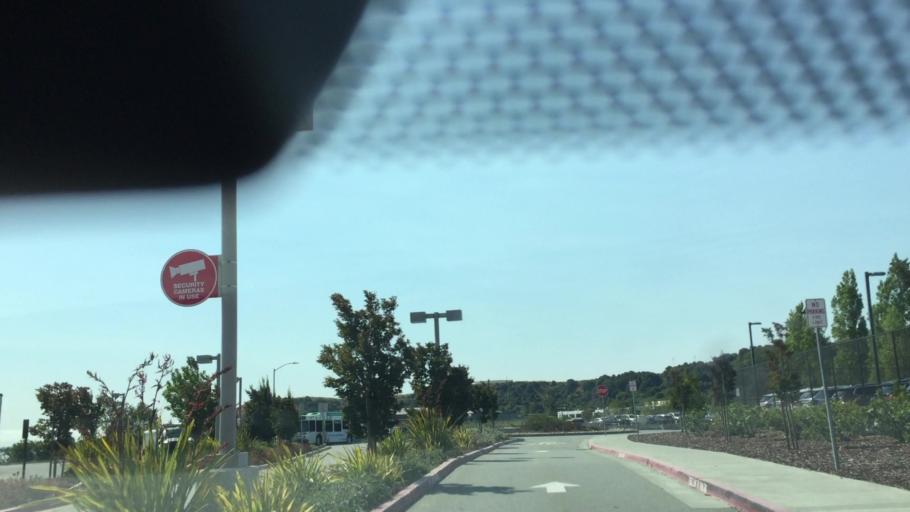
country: US
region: California
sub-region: Marin County
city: San Rafael
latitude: 37.9543
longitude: -122.4907
